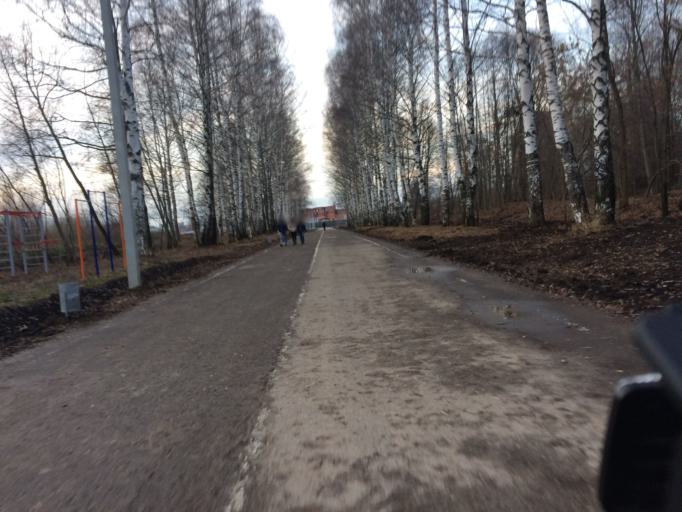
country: RU
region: Mariy-El
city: Yoshkar-Ola
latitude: 56.6246
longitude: 47.9107
